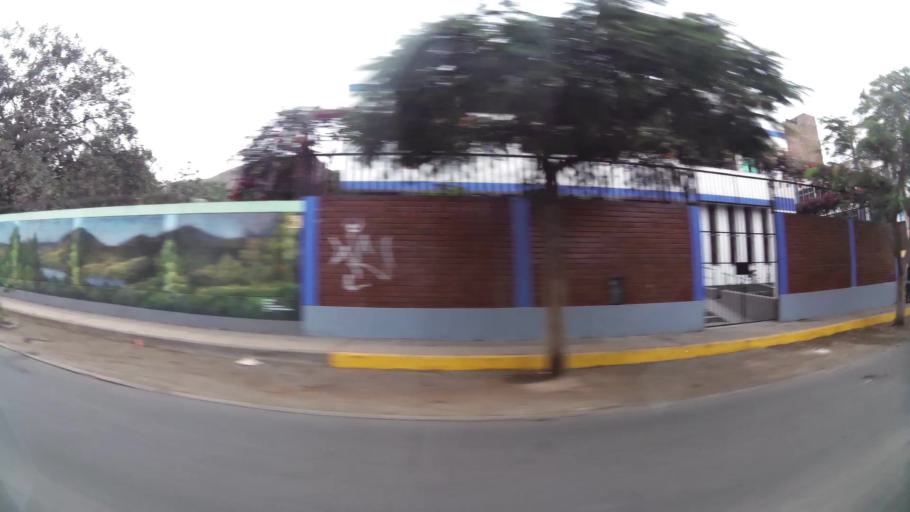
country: PE
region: Lima
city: Lima
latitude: -12.0172
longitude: -76.9833
